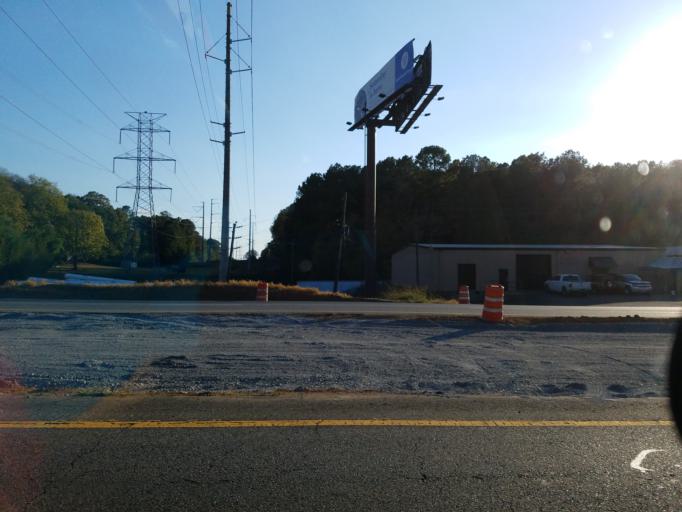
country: US
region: Georgia
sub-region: Bartow County
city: Cartersville
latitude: 34.2029
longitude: -84.8057
